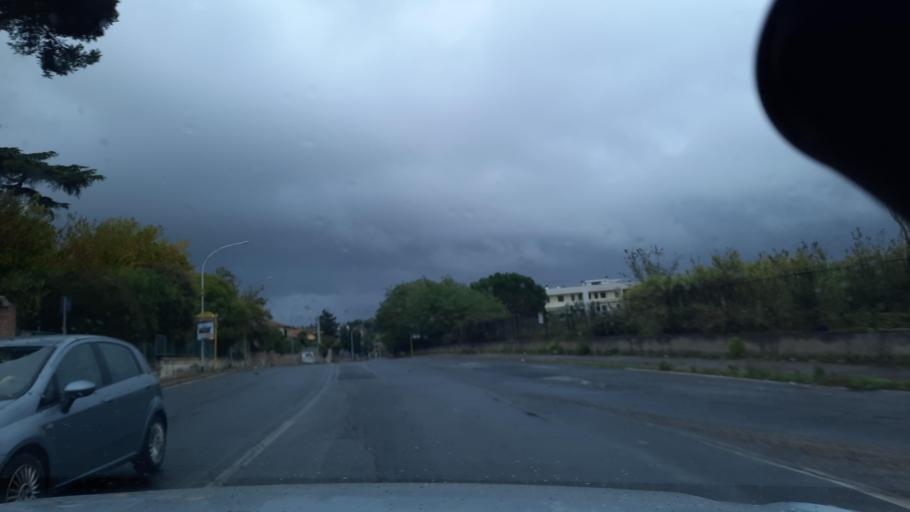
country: IT
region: Latium
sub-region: Citta metropolitana di Roma Capitale
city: Ponte Galeria-La Pisana
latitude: 41.8199
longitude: 12.3497
